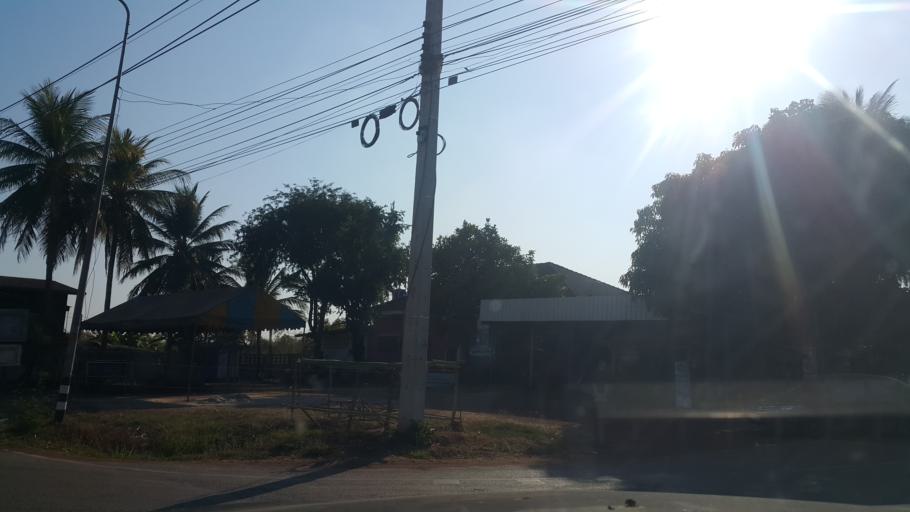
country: TH
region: Changwat Udon Thani
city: Ku Kaeo
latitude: 17.2555
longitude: 103.1164
